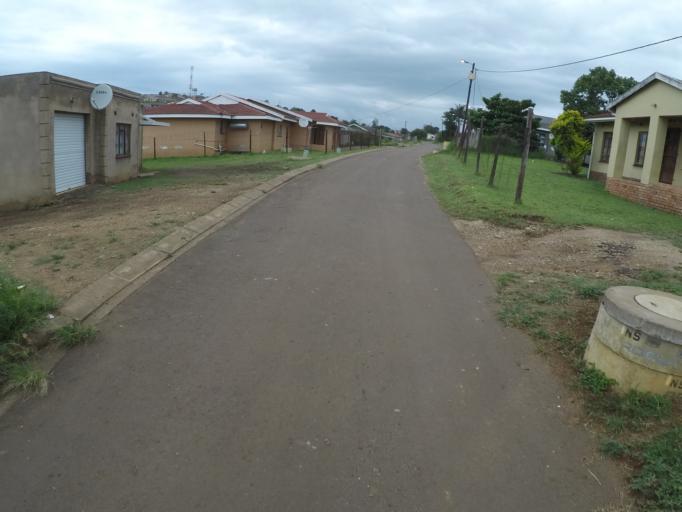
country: ZA
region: KwaZulu-Natal
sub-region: uThungulu District Municipality
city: Empangeni
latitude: -28.7817
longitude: 31.8609
